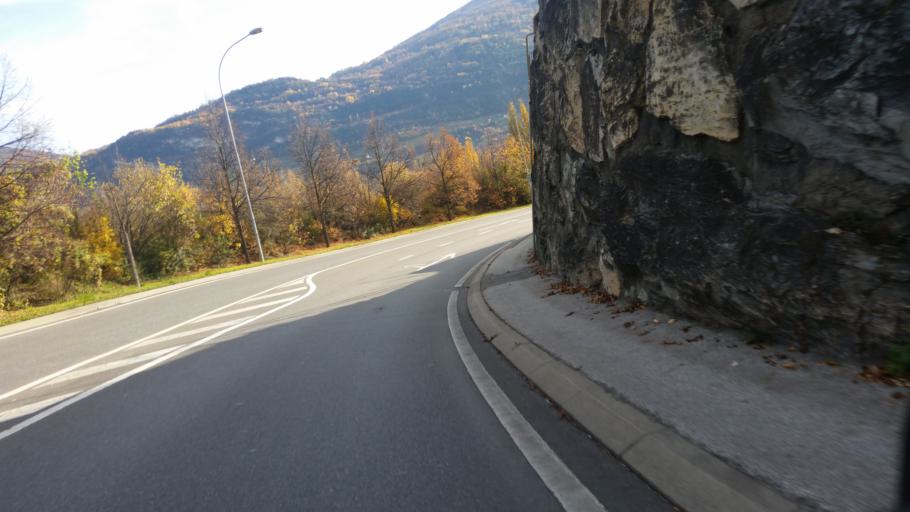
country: CH
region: Valais
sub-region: Sion District
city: Sitten
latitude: 46.2403
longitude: 7.3736
